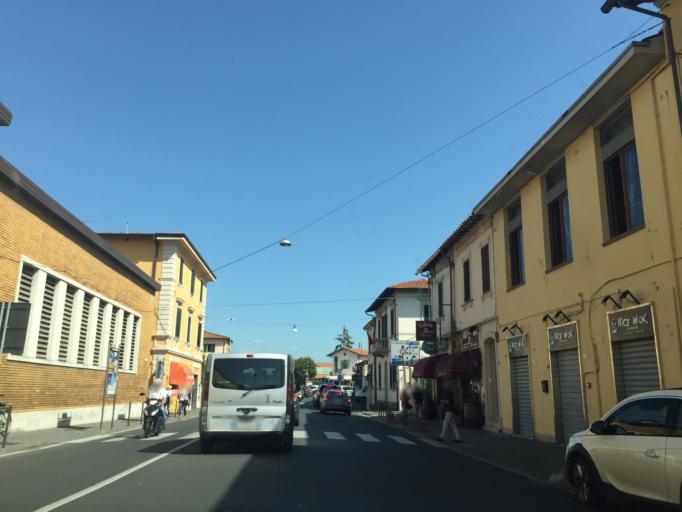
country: IT
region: Tuscany
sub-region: Province of Pisa
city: Pisa
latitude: 43.7241
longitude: 10.3917
